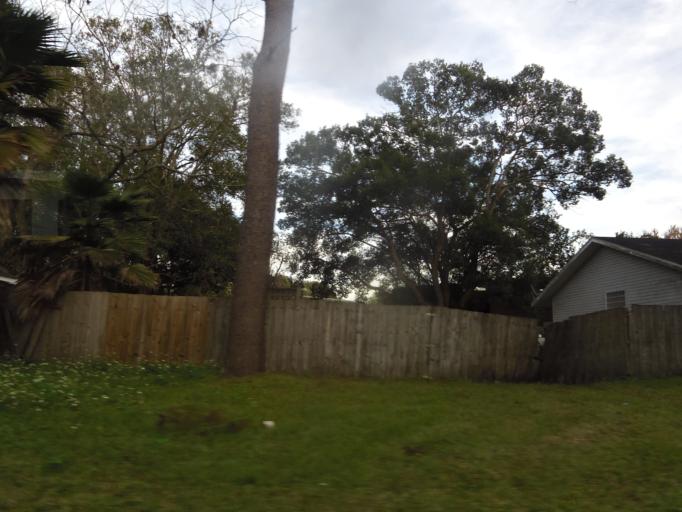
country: US
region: Florida
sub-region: Duval County
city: Jacksonville
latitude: 30.3382
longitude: -81.7162
